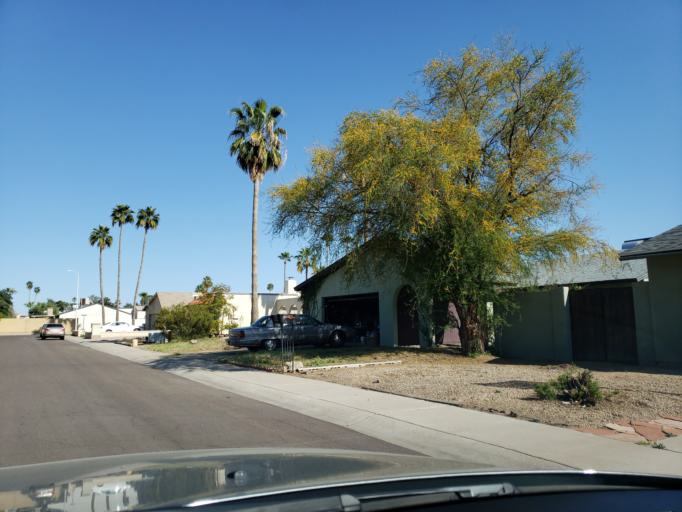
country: US
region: Arizona
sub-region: Maricopa County
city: Glendale
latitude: 33.5734
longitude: -112.1770
